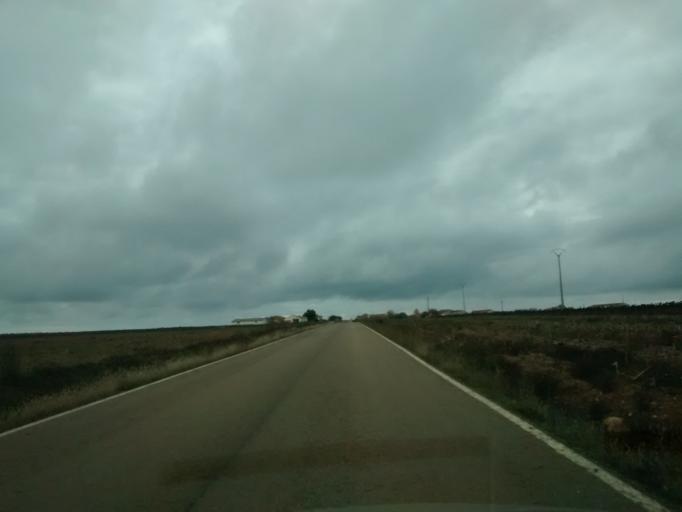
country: ES
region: Aragon
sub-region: Provincia de Zaragoza
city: Torralba de los Frailes
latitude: 41.0380
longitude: -1.6523
